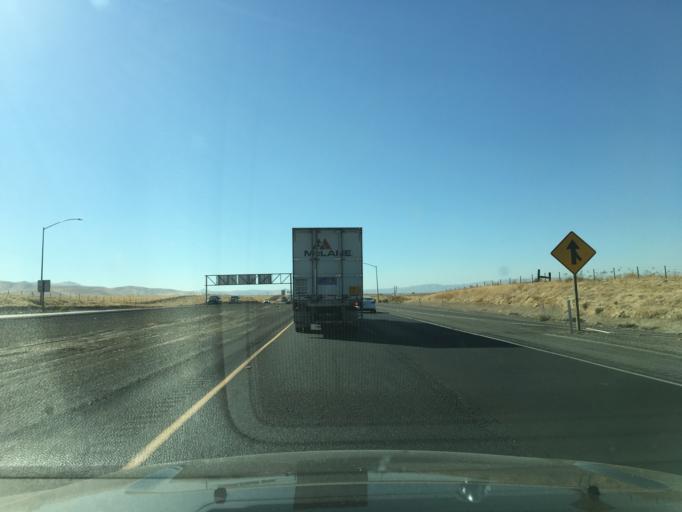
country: US
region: California
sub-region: Merced County
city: Los Banos
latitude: 37.0568
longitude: -120.9724
